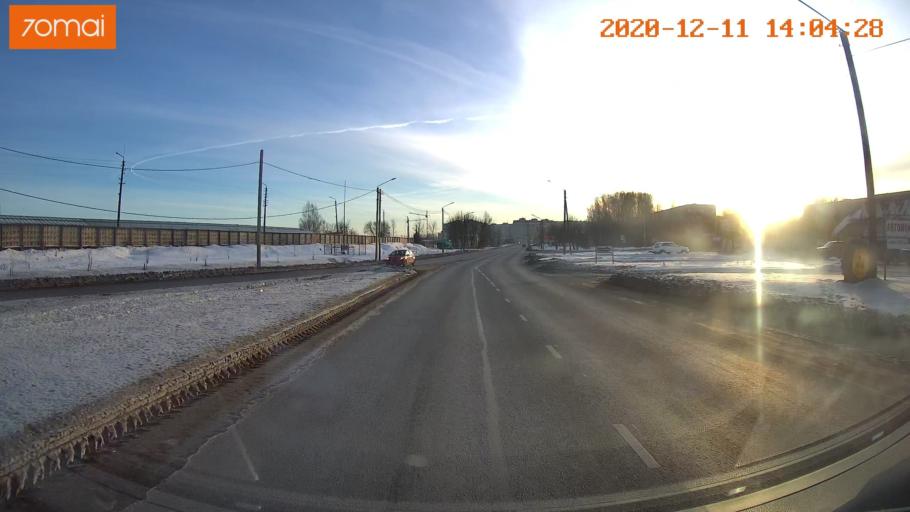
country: RU
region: Kostroma
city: Oktyabr'skiy
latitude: 57.7552
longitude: 41.0163
